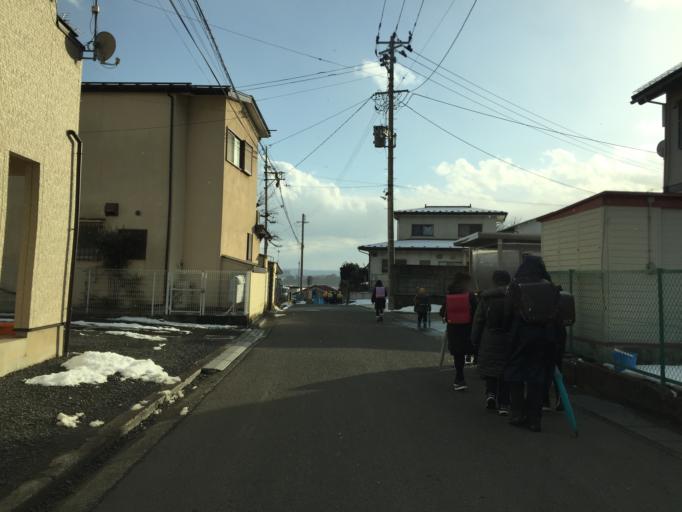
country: JP
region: Fukushima
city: Fukushima-shi
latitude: 37.8306
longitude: 140.4501
